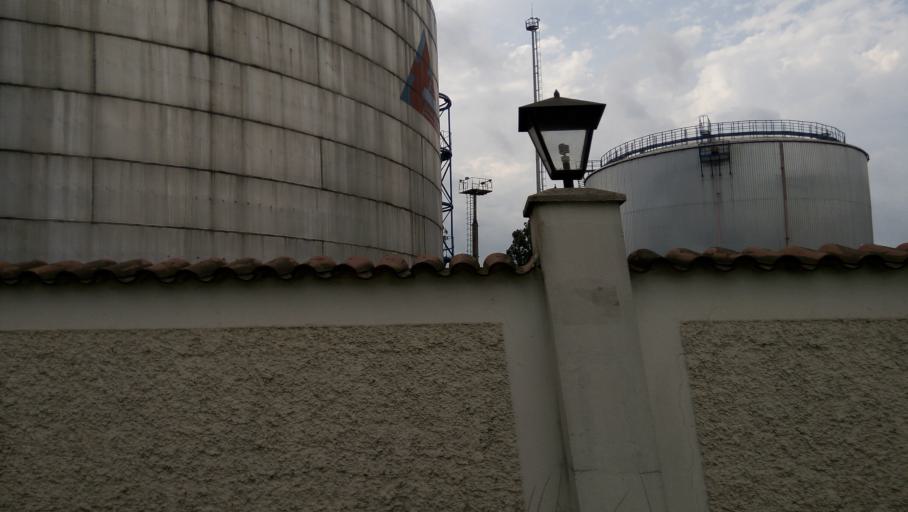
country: GE
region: Ajaria
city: Batumi
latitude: 41.6428
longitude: 41.6652
